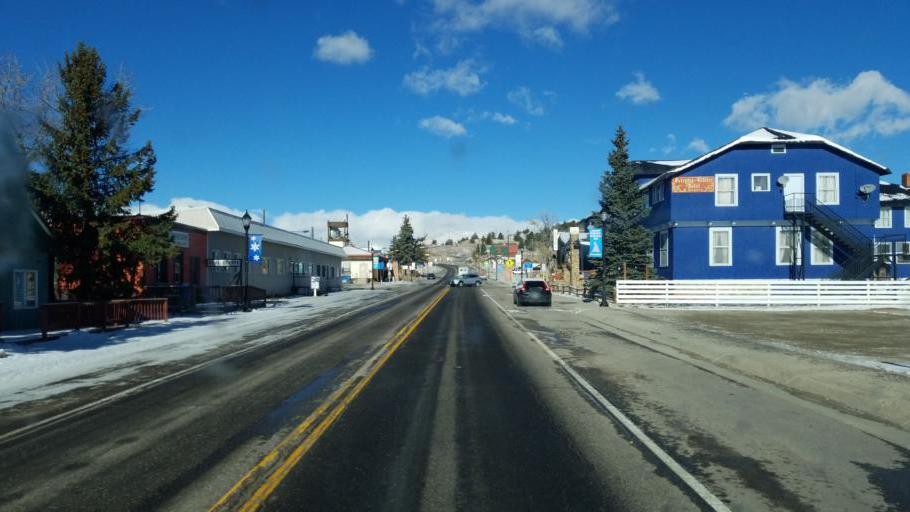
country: US
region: Colorado
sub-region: Park County
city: Fairplay
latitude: 39.2242
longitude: -106.0010
